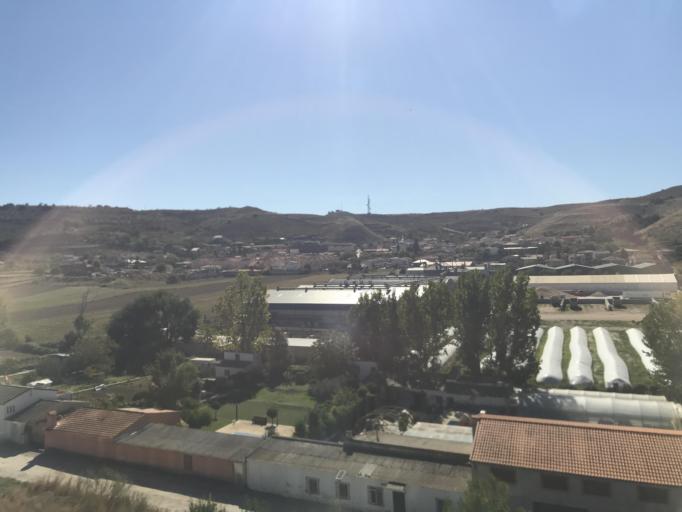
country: ES
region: Madrid
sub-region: Provincia de Madrid
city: Anchuelo
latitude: 40.4715
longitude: -3.2708
